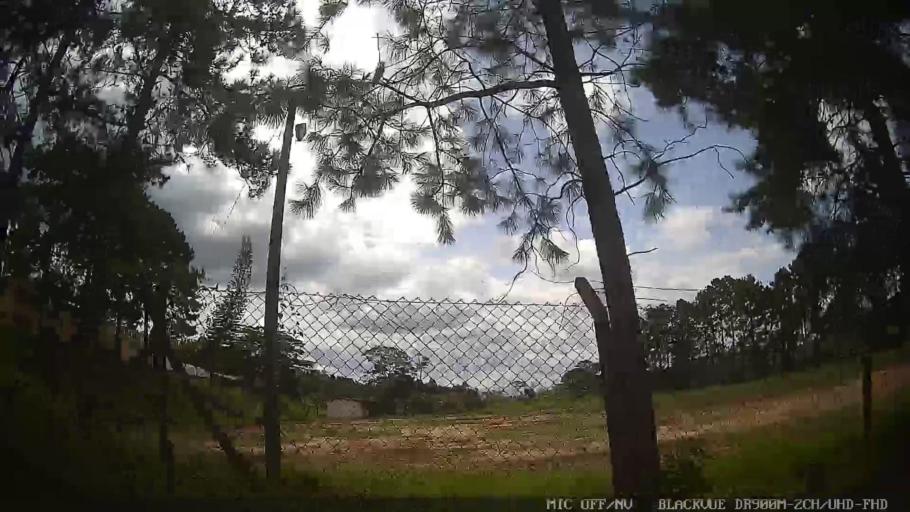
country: BR
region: Sao Paulo
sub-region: Suzano
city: Suzano
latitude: -23.6487
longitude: -46.2411
